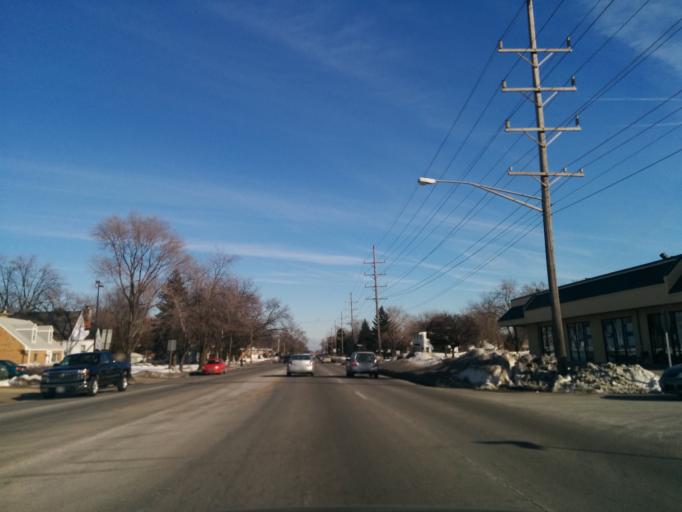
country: US
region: Illinois
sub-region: Cook County
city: Northlake
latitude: 41.9308
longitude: -87.9031
